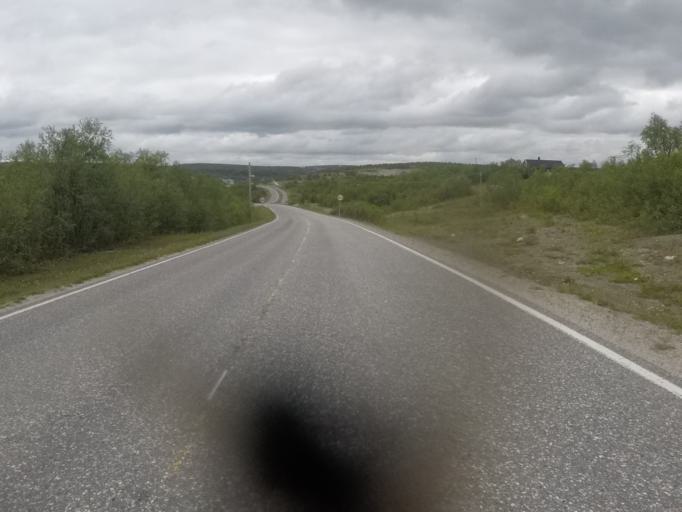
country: NO
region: Finnmark Fylke
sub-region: Kautokeino
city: Kautokeino
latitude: 68.9851
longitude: 23.0531
